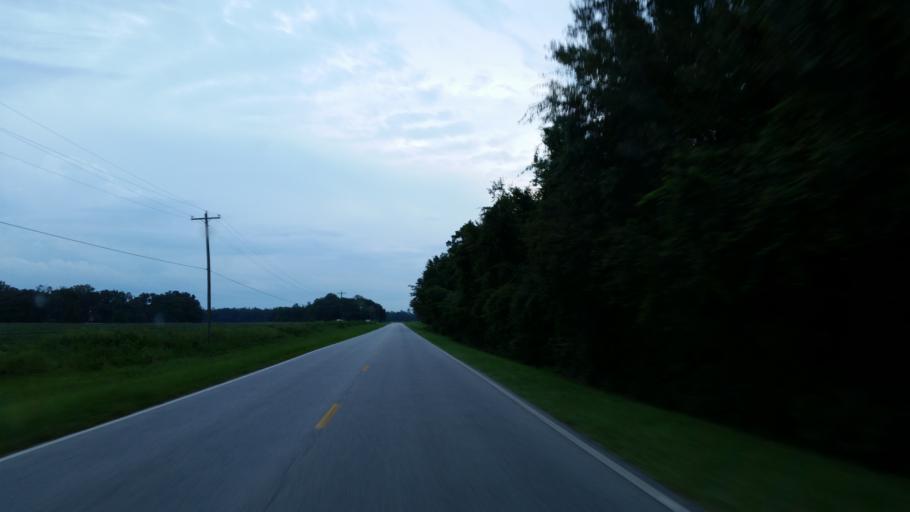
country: US
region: Georgia
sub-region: Echols County
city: Statenville
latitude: 30.6626
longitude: -83.1843
